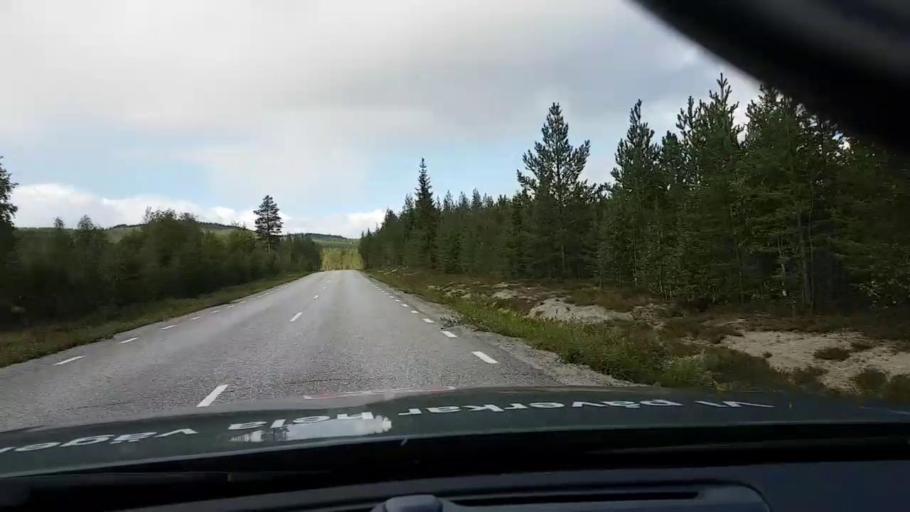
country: SE
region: Vaesternorrland
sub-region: OErnskoeldsviks Kommun
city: Bredbyn
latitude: 63.6818
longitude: 17.7825
